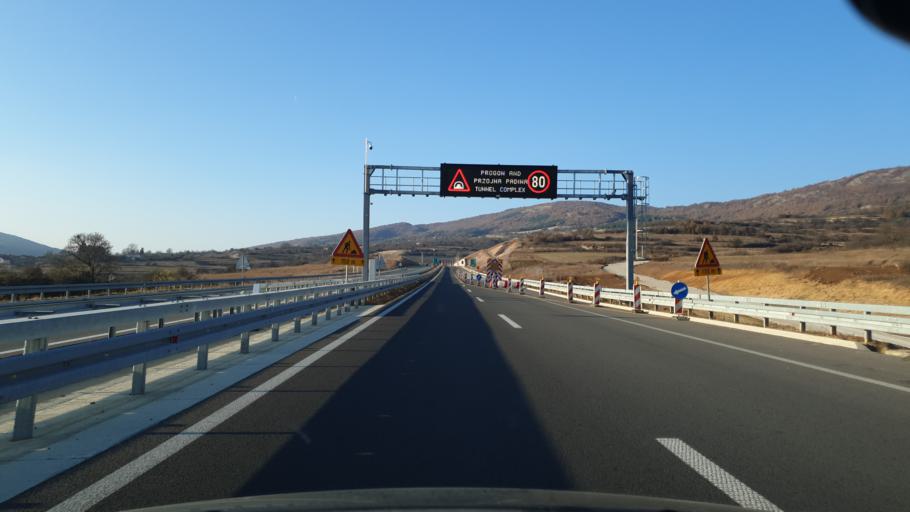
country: RS
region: Central Serbia
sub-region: Pirotski Okrug
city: Dimitrovgrad
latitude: 43.0166
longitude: 22.8003
